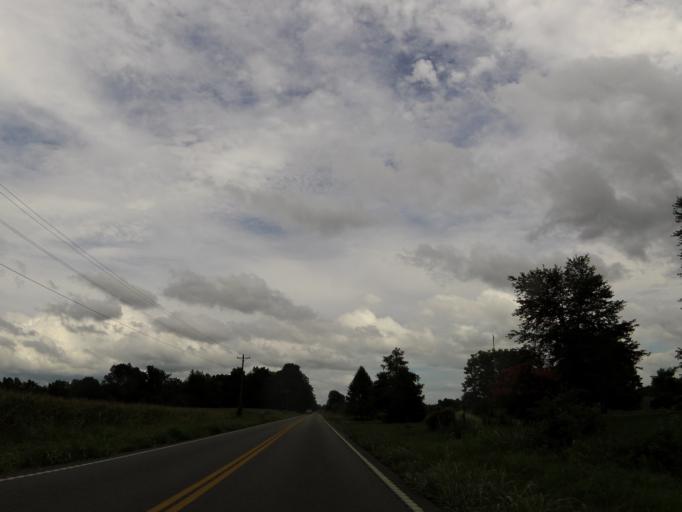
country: US
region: Kentucky
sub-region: Ballard County
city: La Center
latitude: 36.9894
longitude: -88.9640
